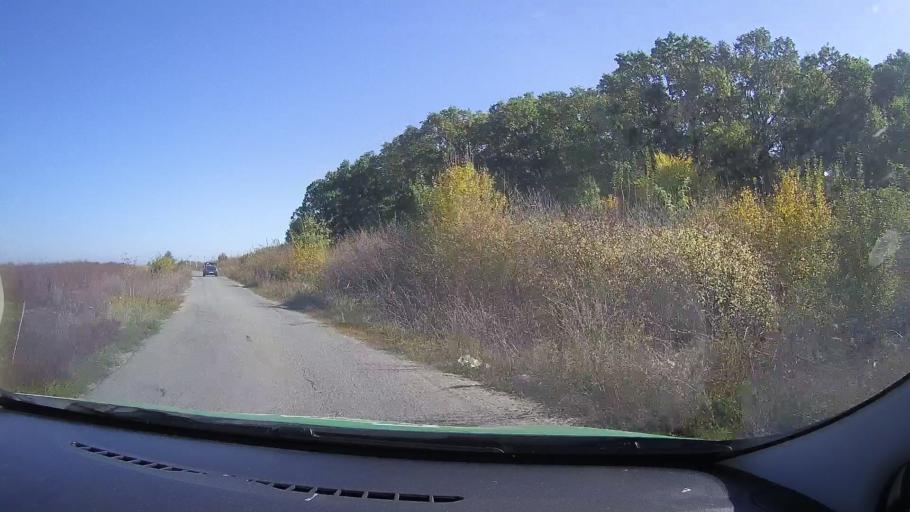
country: RO
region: Satu Mare
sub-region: Comuna Doba
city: Doba
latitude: 47.7180
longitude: 22.7290
